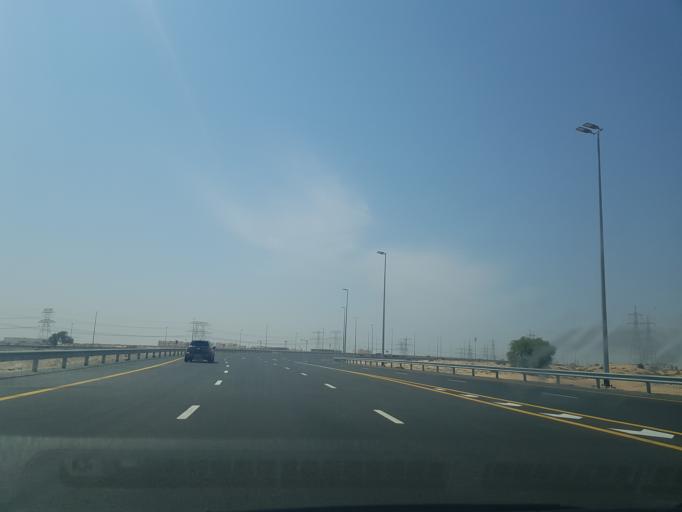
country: AE
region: Ash Shariqah
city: Sharjah
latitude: 25.2414
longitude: 55.5643
